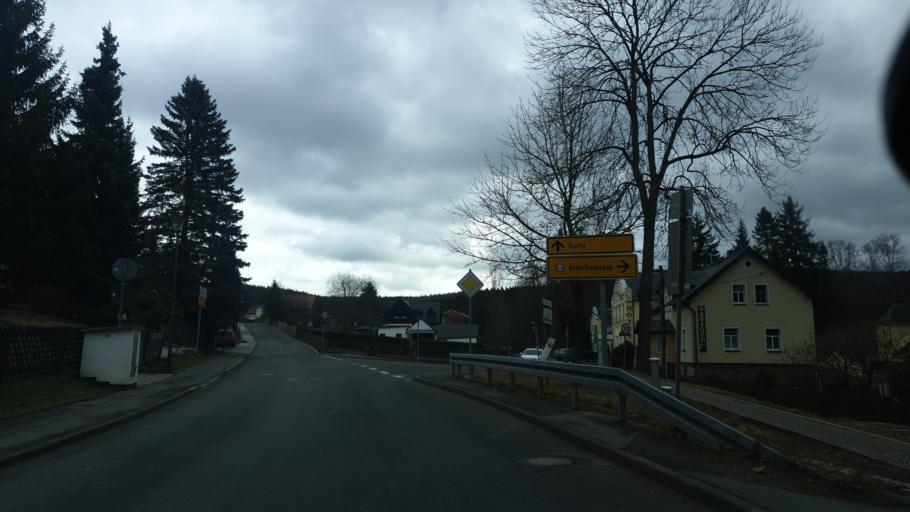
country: DE
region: Saxony
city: Bad Elster
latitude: 50.2757
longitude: 12.2463
